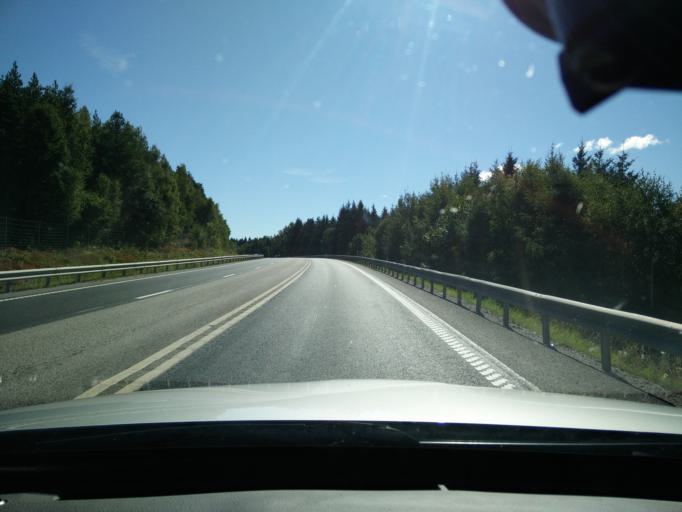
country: SE
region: Stockholm
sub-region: Lidingo
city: Lidingoe
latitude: 59.4539
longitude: 18.1777
